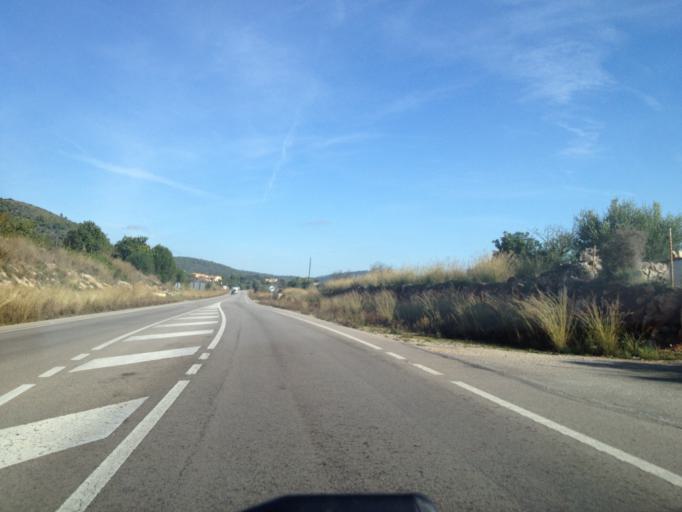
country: ES
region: Balearic Islands
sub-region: Illes Balears
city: Son Servera
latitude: 39.6384
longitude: 3.3700
